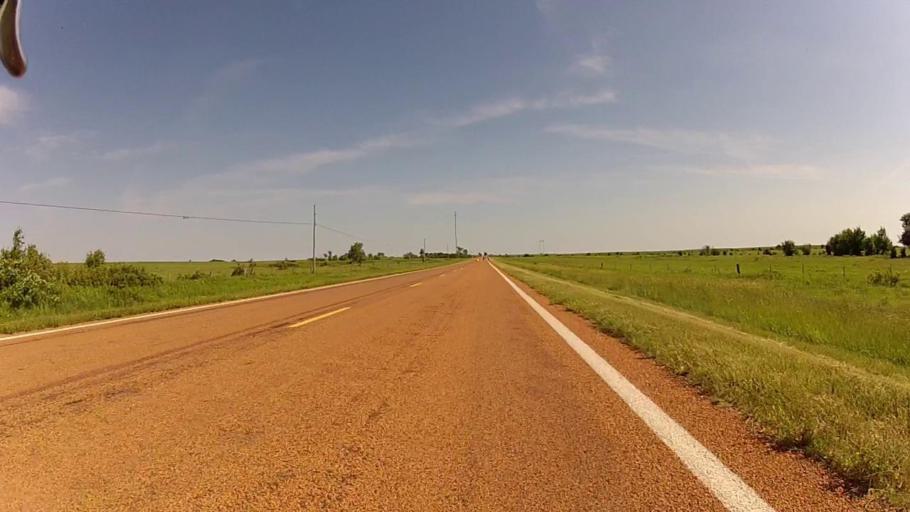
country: US
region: Kansas
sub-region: Cowley County
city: Winfield
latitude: 37.1039
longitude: -96.6436
